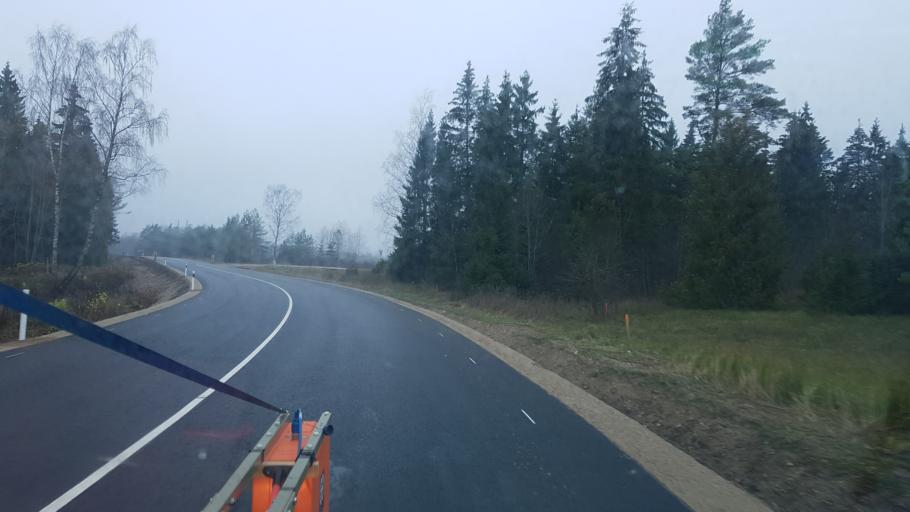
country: EE
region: Raplamaa
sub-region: Kohila vald
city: Kohila
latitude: 59.1784
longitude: 24.8235
